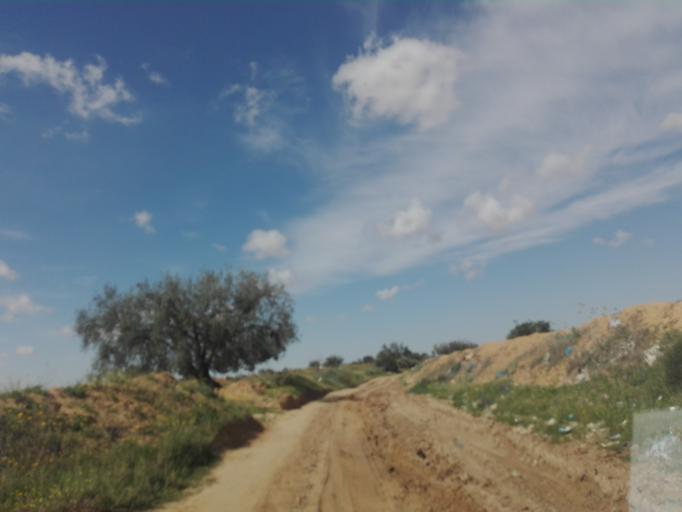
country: TN
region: Safaqis
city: Sfax
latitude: 34.7349
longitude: 10.5177
